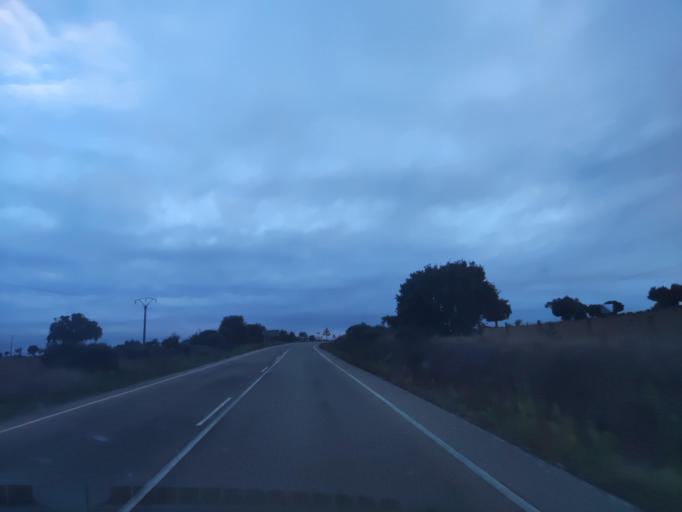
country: ES
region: Castille and Leon
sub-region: Provincia de Salamanca
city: Ahigal de los Aceiteros
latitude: 40.8832
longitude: -6.7149
